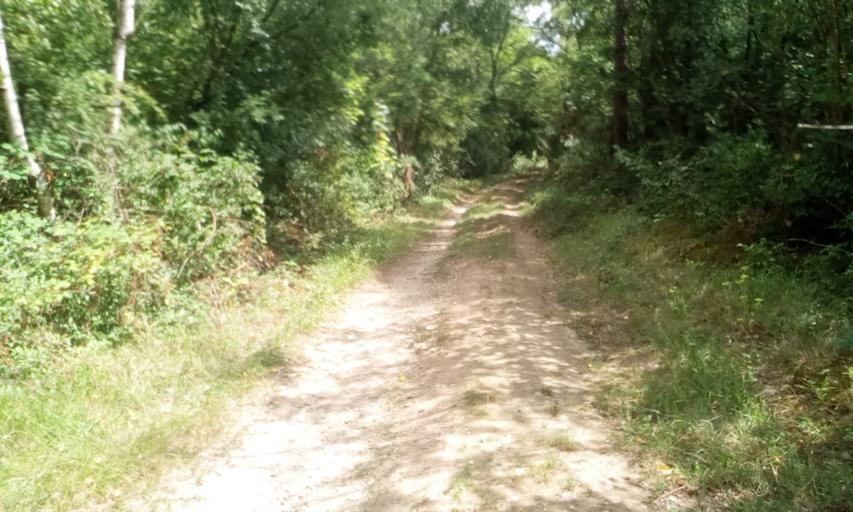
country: FR
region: Lower Normandy
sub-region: Departement du Calvados
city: Cagny
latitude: 49.1130
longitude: -0.2524
